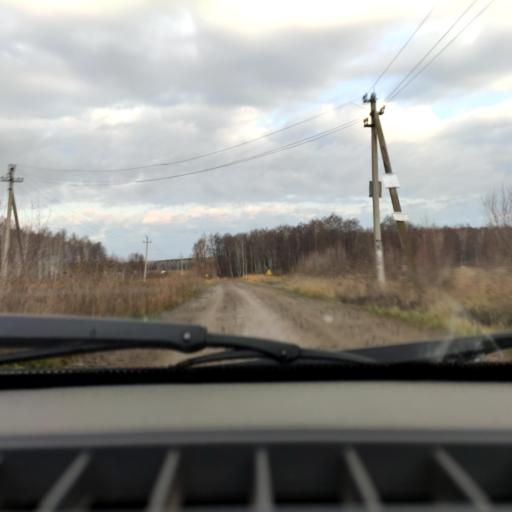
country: RU
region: Bashkortostan
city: Avdon
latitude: 54.6322
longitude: 55.7325
